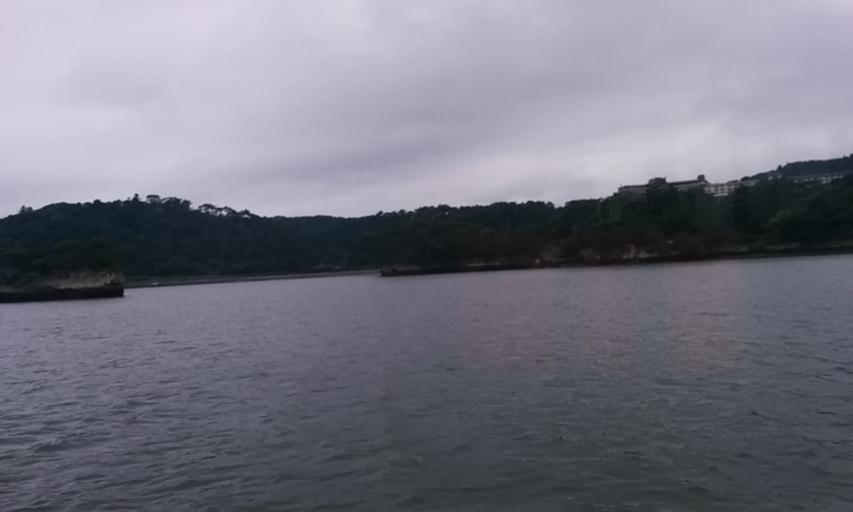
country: JP
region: Miyagi
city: Matsushima
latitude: 38.3660
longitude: 141.0653
